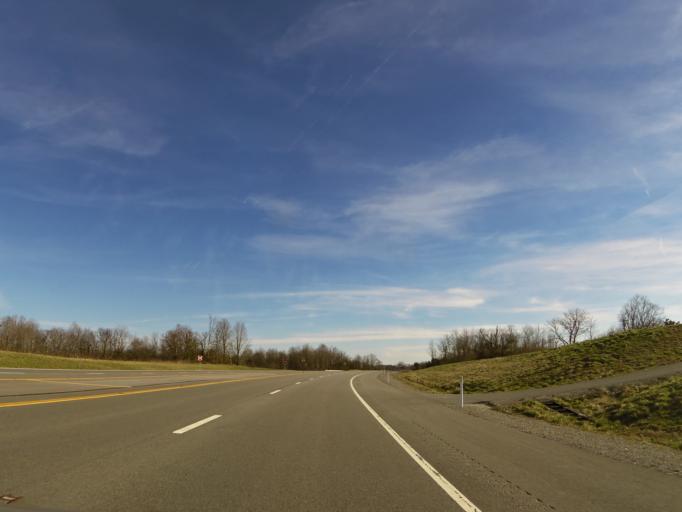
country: US
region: Tennessee
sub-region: Cannon County
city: Woodbury
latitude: 35.7974
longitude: -85.9969
